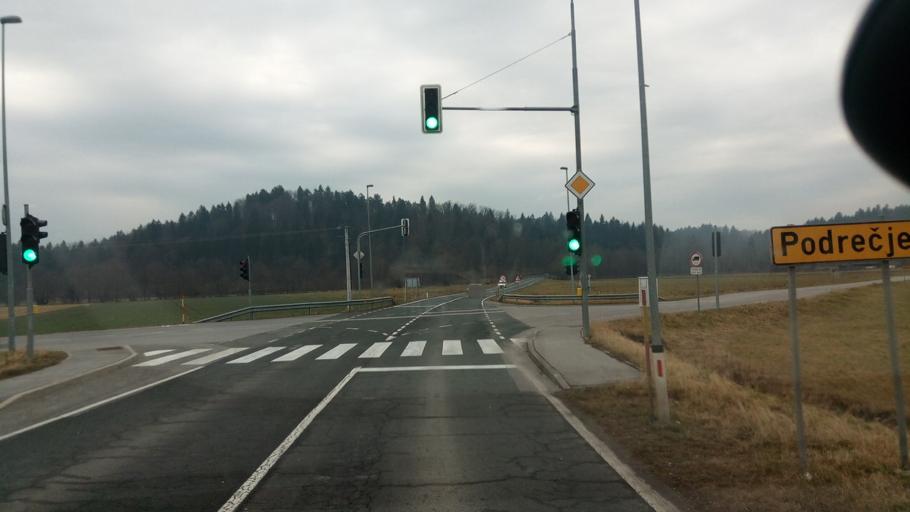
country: SI
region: Domzale
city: Vir
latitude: 46.1471
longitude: 14.6175
